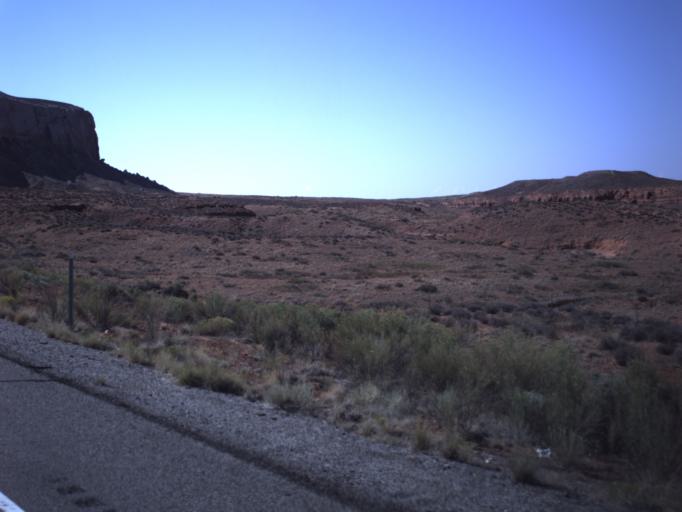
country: US
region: Utah
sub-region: San Juan County
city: Blanding
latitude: 37.2440
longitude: -109.6077
